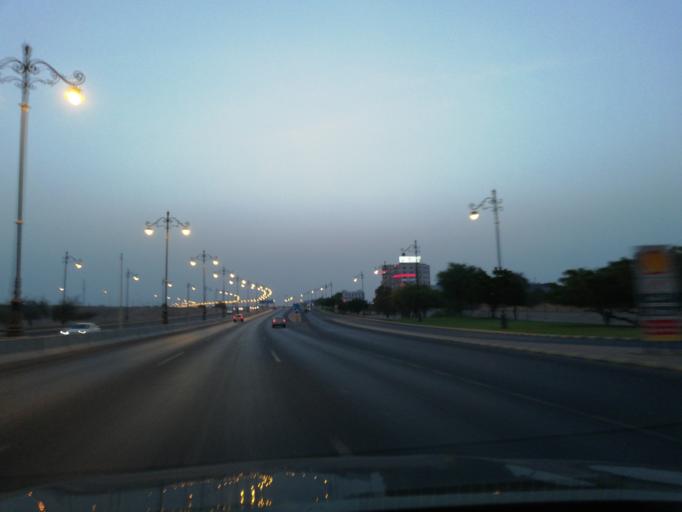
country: OM
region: Muhafazat Masqat
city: Bawshar
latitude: 23.5900
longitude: 58.3547
